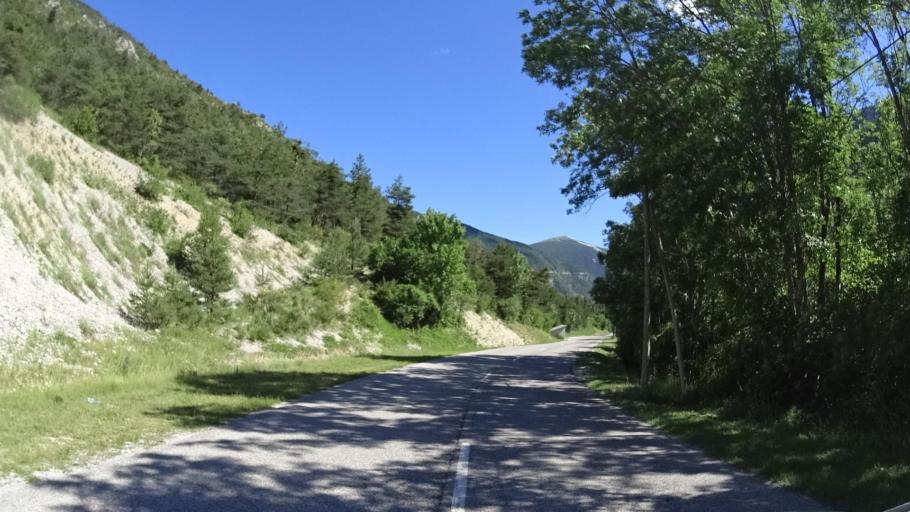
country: FR
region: Provence-Alpes-Cote d'Azur
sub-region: Departement des Alpes-de-Haute-Provence
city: Annot
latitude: 44.0821
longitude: 6.5677
